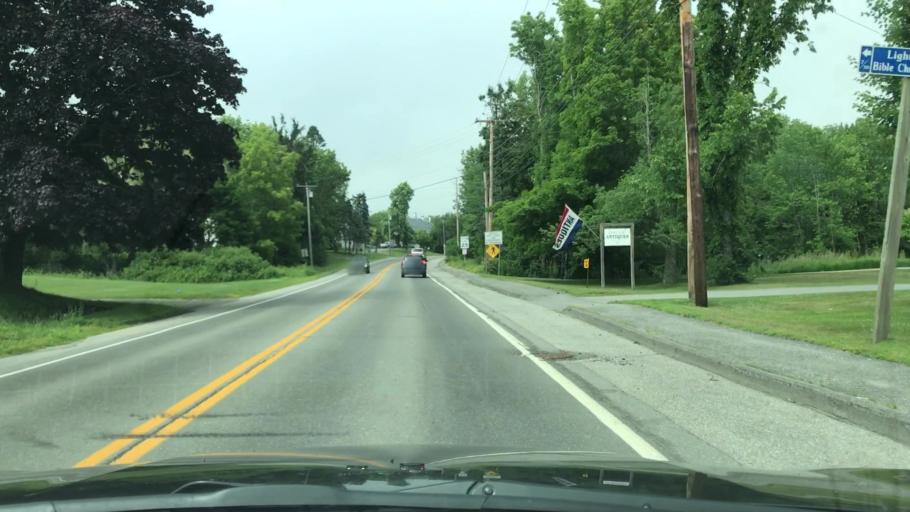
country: US
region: Maine
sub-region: Waldo County
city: Belfast
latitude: 44.4535
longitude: -68.9319
